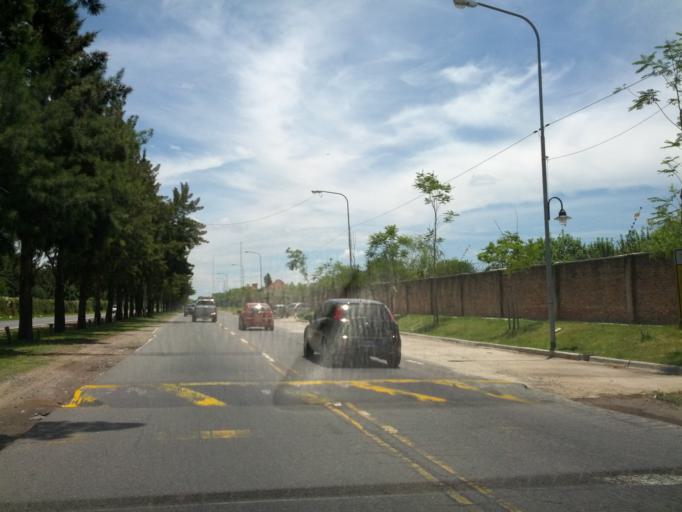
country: AR
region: Buenos Aires
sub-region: Partido de Tigre
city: Tigre
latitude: -34.4701
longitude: -58.6087
